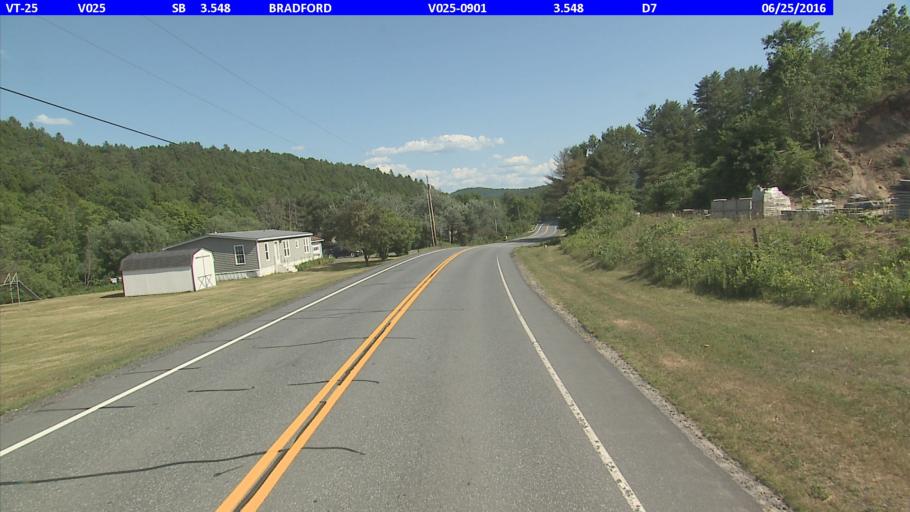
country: US
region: New Hampshire
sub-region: Grafton County
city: Orford
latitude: 44.0055
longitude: -72.1638
